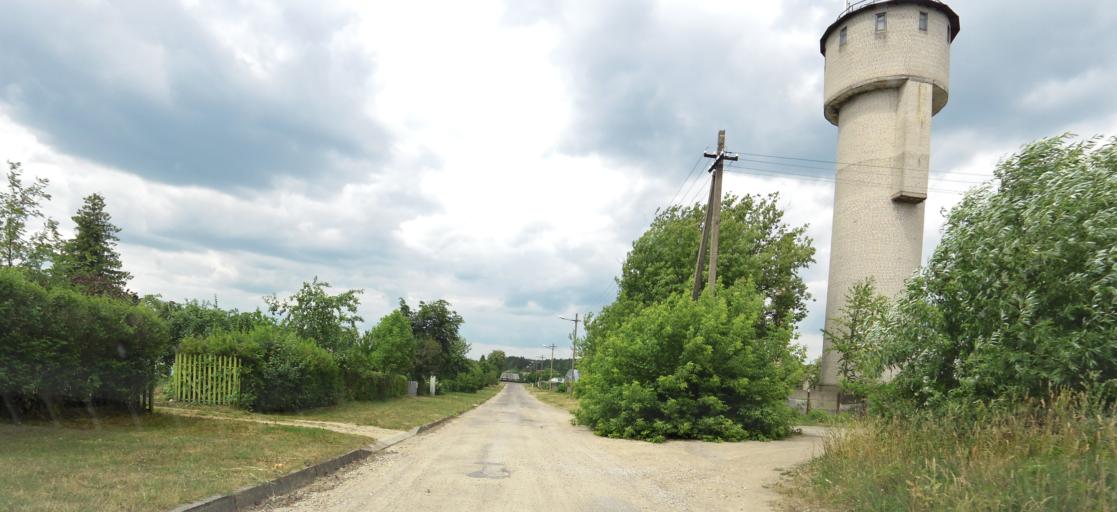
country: LT
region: Vilnius County
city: Ukmerge
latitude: 55.2116
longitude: 24.7903
